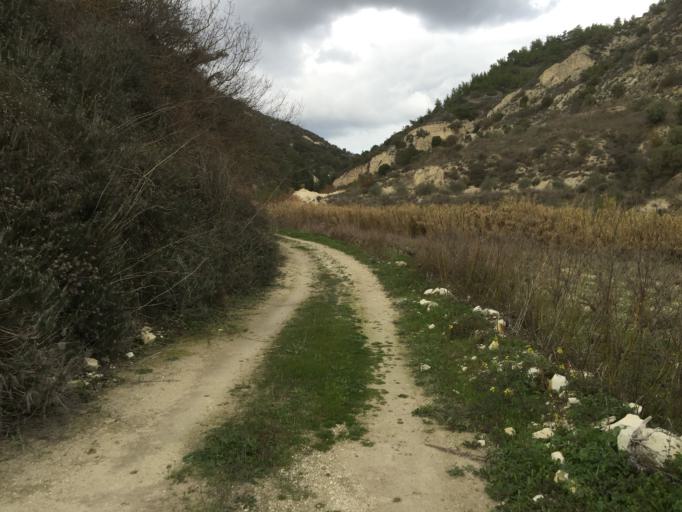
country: CY
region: Pafos
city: Mesogi
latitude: 34.8237
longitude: 32.5208
